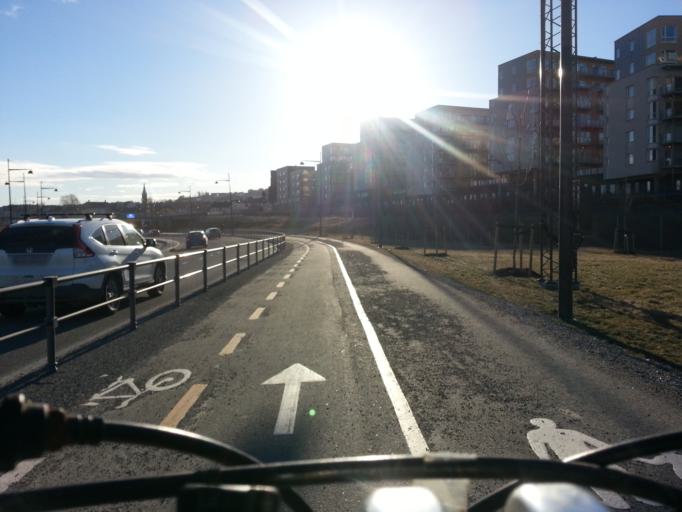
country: NO
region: Sor-Trondelag
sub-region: Trondheim
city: Trondheim
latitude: 63.4374
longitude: 10.4112
